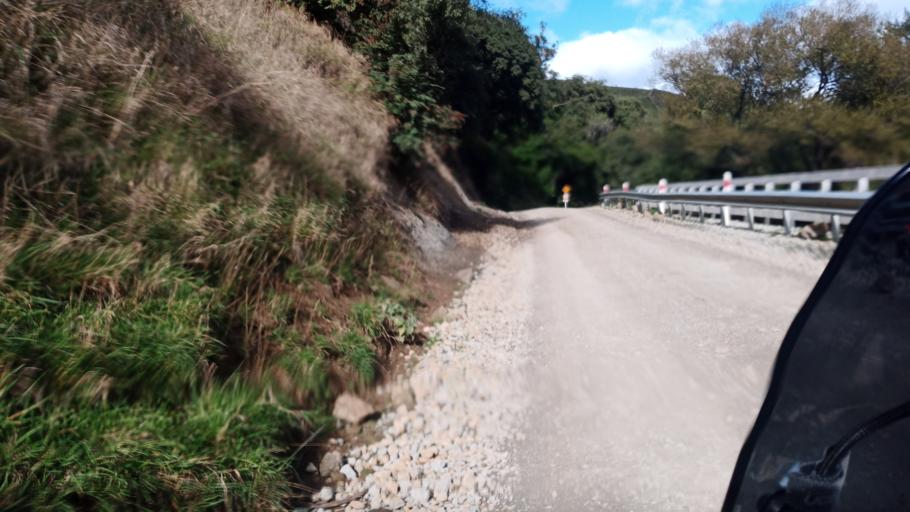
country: NZ
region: Gisborne
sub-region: Gisborne District
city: Gisborne
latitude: -38.5343
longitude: 177.5291
